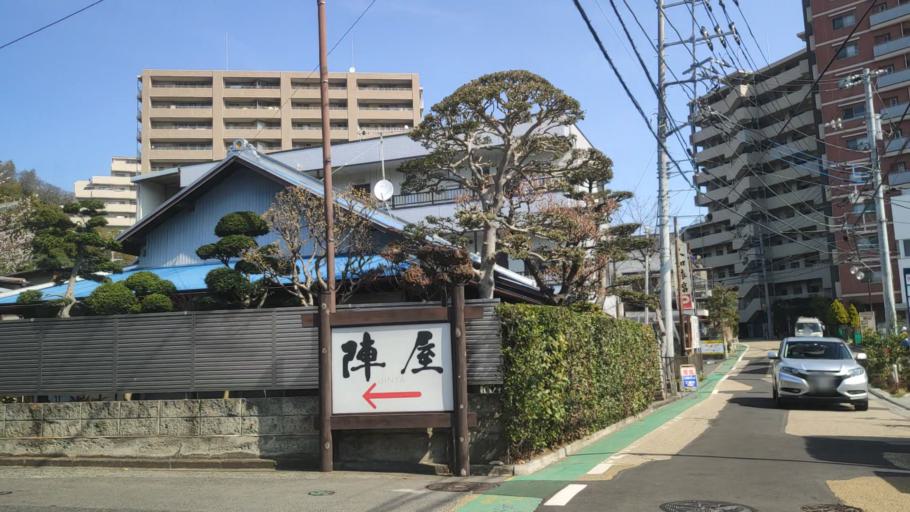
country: JP
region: Kanagawa
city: Isehara
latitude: 35.3824
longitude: 139.2768
